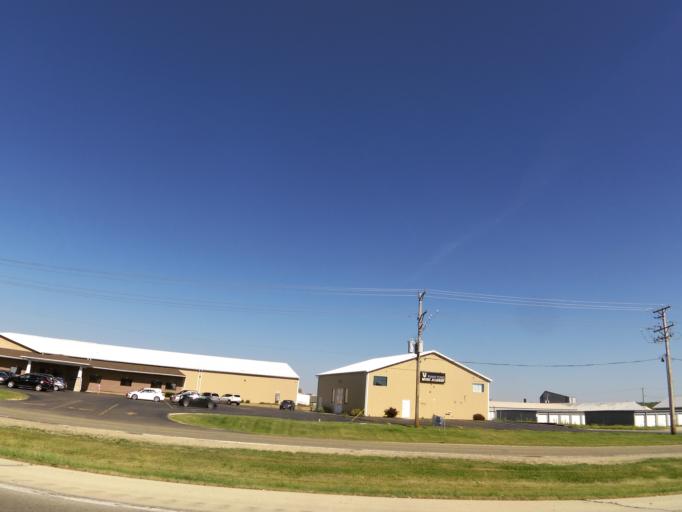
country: US
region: Illinois
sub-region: Winnebago County
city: Roscoe
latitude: 42.3977
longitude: -89.0130
